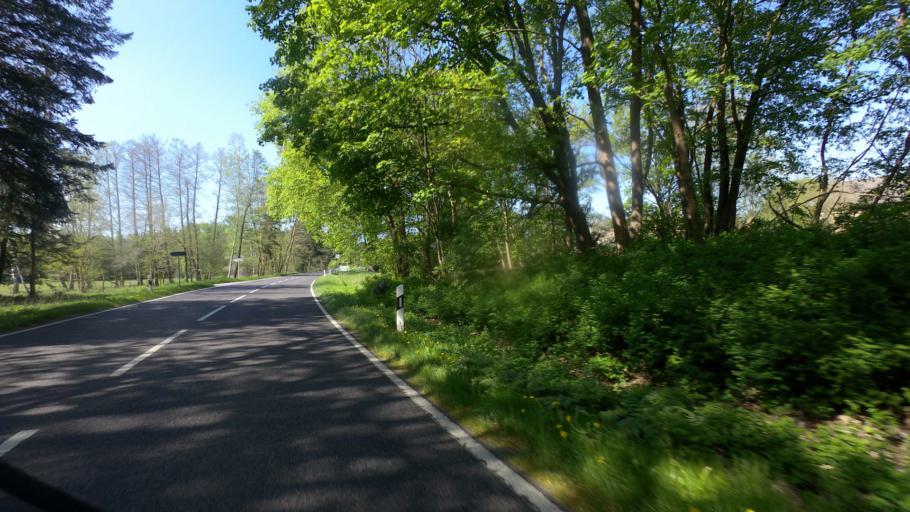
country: DE
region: Brandenburg
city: Halbe
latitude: 52.1524
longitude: 13.7419
